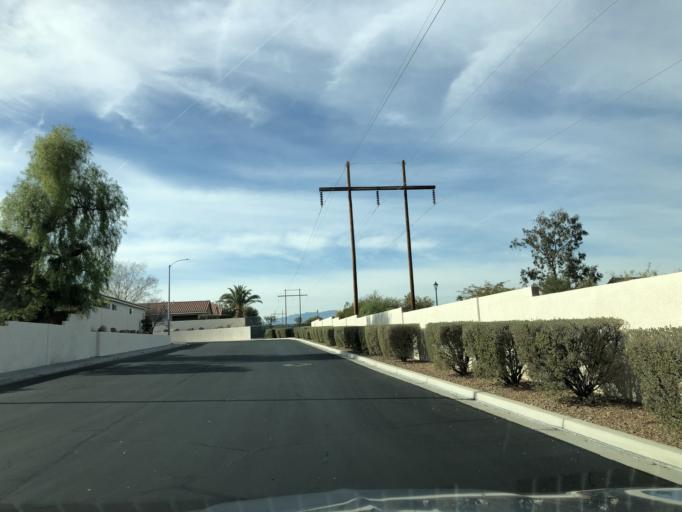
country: US
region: Nevada
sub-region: Clark County
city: Whitney
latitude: 36.0169
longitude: -115.0858
